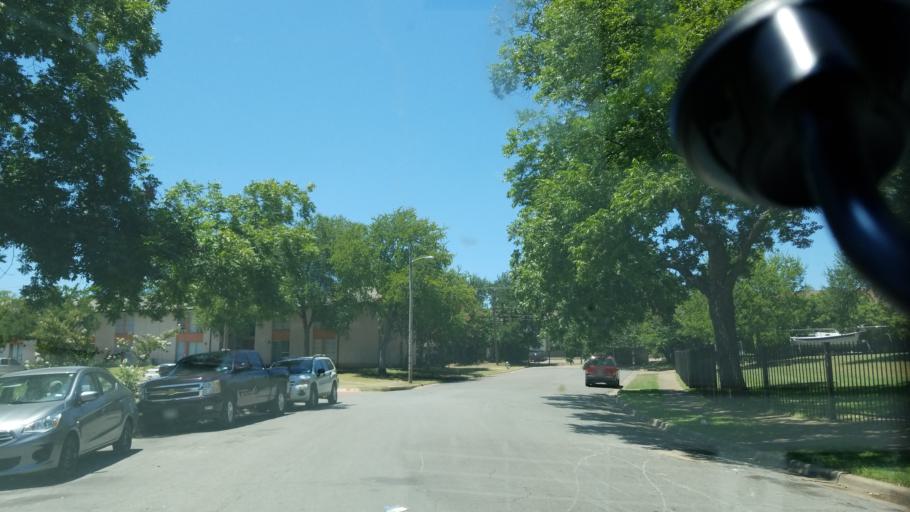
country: US
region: Texas
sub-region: Dallas County
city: Cockrell Hill
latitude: 32.6971
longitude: -96.8350
